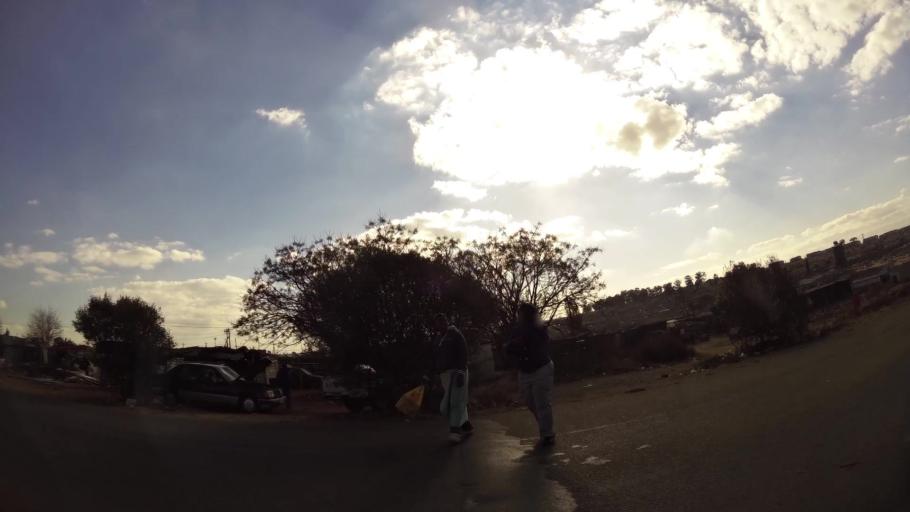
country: ZA
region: Gauteng
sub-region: Ekurhuleni Metropolitan Municipality
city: Tembisa
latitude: -25.9920
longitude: 28.1900
